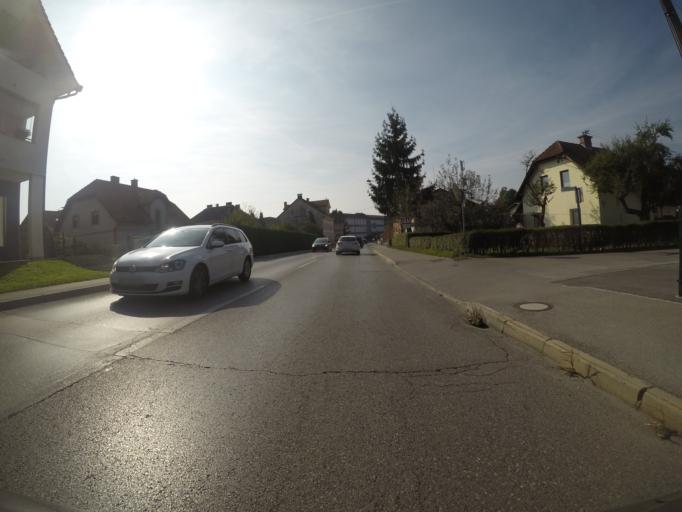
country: SI
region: Kamnik
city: Smarca
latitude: 46.2034
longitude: 14.5970
